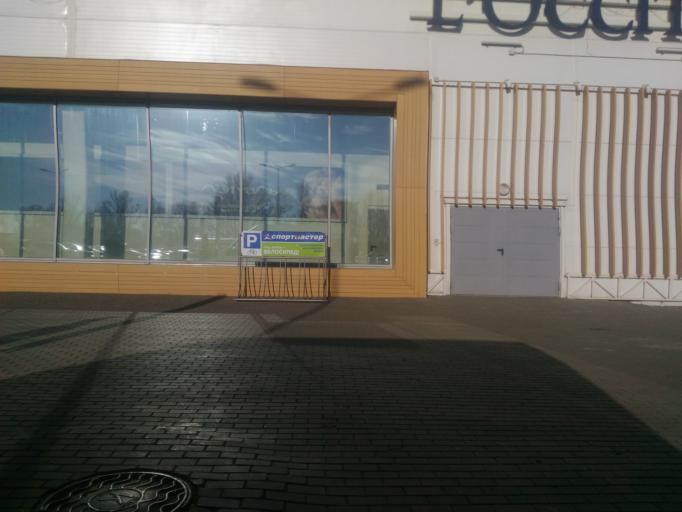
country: RU
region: Ulyanovsk
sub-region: Ulyanovskiy Rayon
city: Ulyanovsk
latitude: 54.3064
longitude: 48.3601
